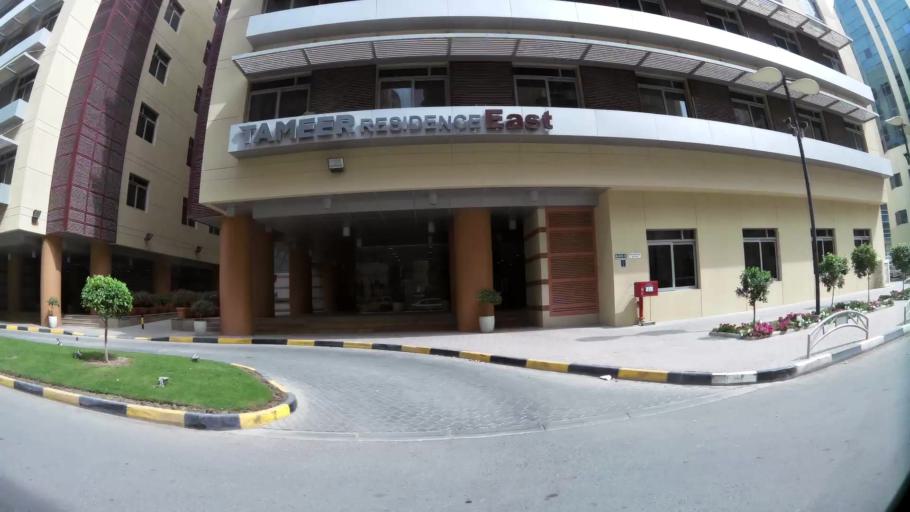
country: QA
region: Baladiyat ad Dawhah
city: Doha
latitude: 25.2899
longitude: 51.5039
